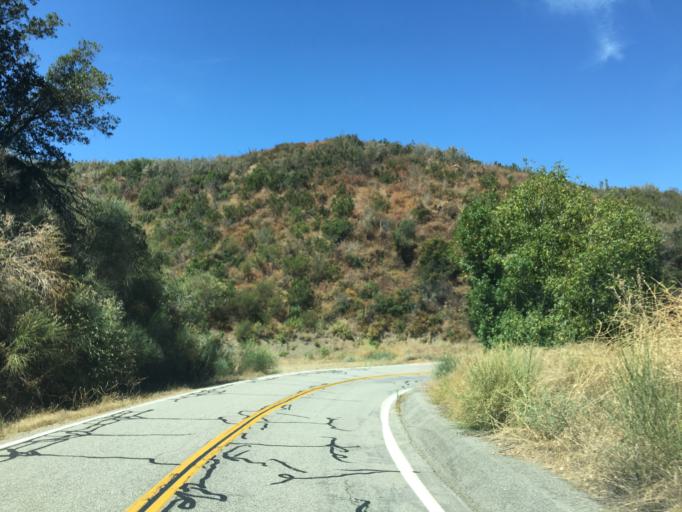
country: US
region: California
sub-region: Los Angeles County
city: Glendora
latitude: 34.1966
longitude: -117.8374
